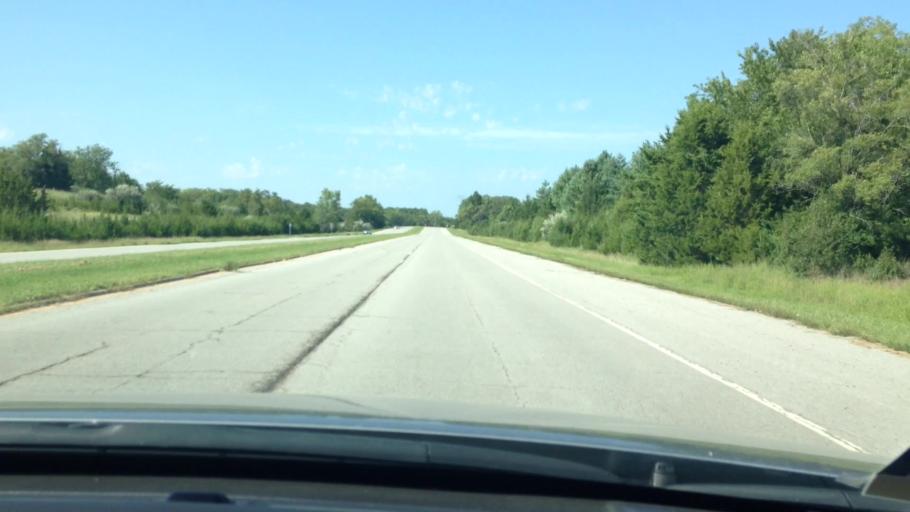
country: US
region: Missouri
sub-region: Jackson County
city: Grandview
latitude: 38.8888
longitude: -94.4941
